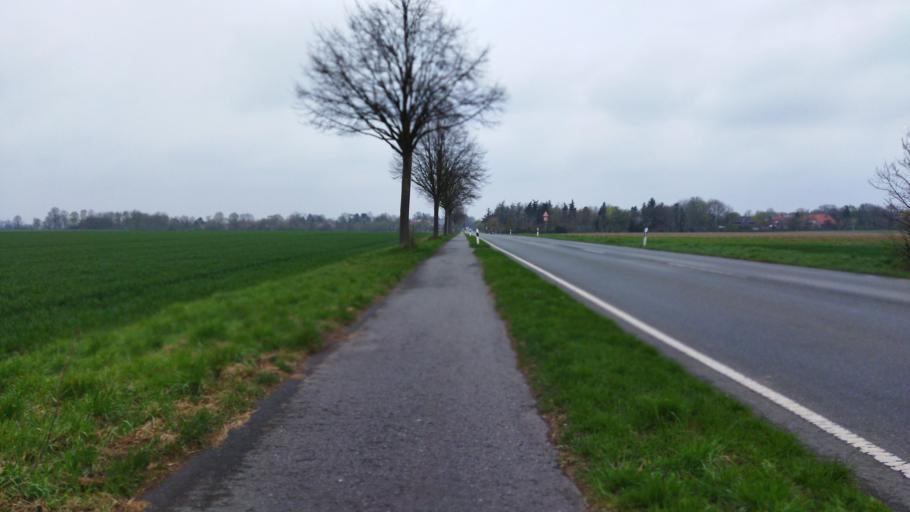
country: DE
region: Lower Saxony
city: Schweringen
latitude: 52.7395
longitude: 9.1842
